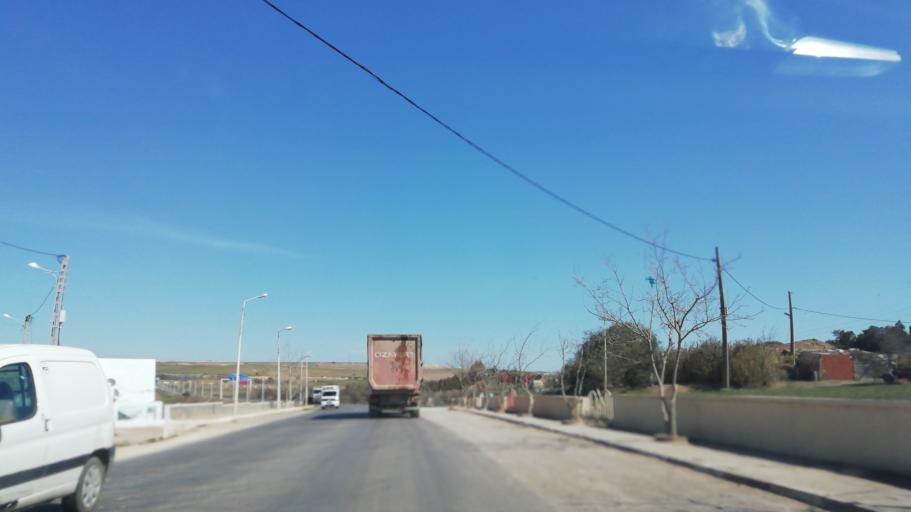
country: DZ
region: Oran
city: Sidi ech Chahmi
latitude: 35.5641
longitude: -0.5619
